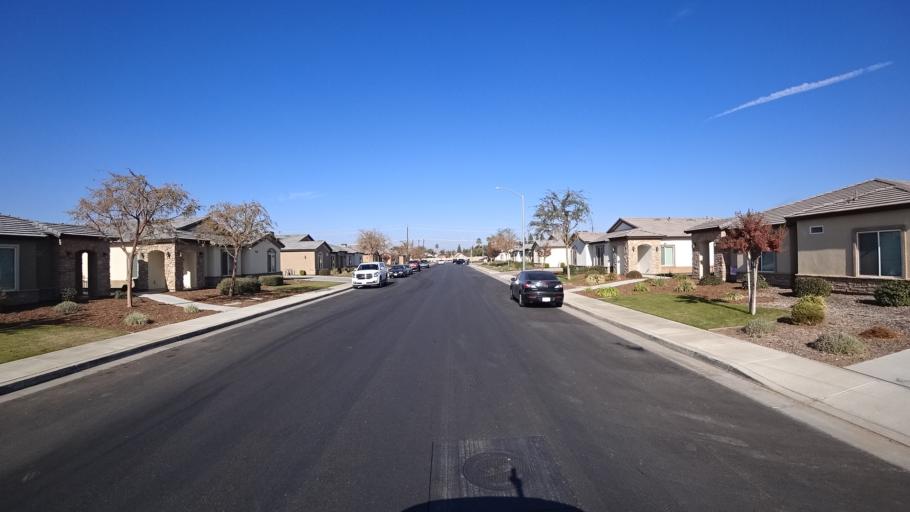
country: US
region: California
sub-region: Kern County
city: Greenfield
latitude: 35.2942
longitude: -119.0617
